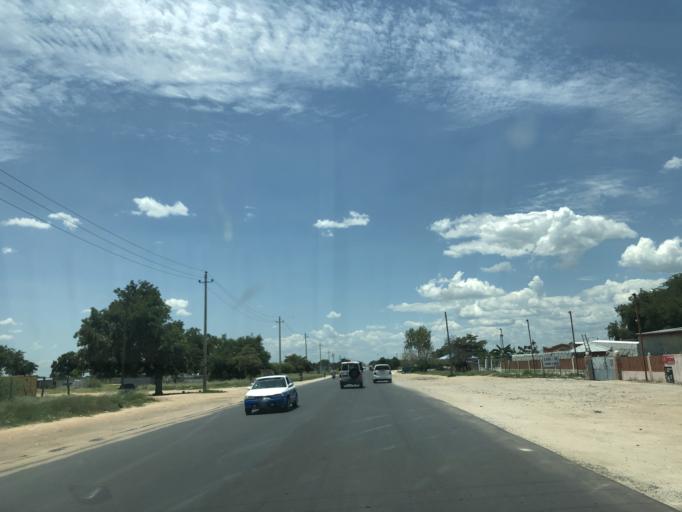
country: AO
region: Cunene
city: Ondjiva
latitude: -17.0492
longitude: 15.7442
